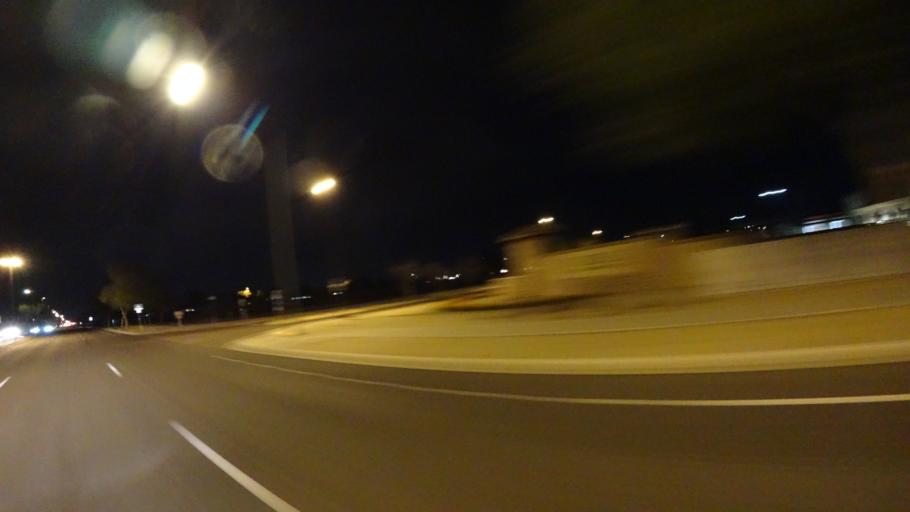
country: US
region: Arizona
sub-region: Maricopa County
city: Queen Creek
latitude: 33.2362
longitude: -111.7205
